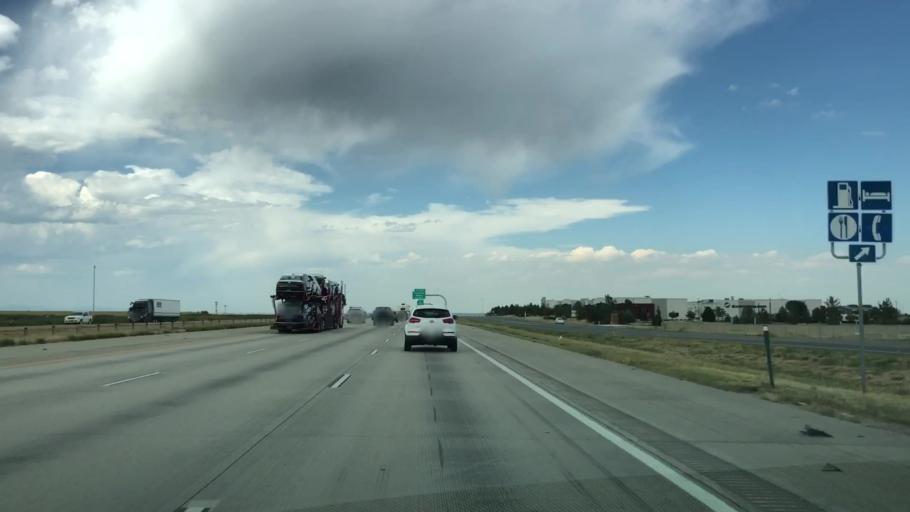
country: US
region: Colorado
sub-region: Weld County
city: Dacono
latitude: 40.0716
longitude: -104.9800
